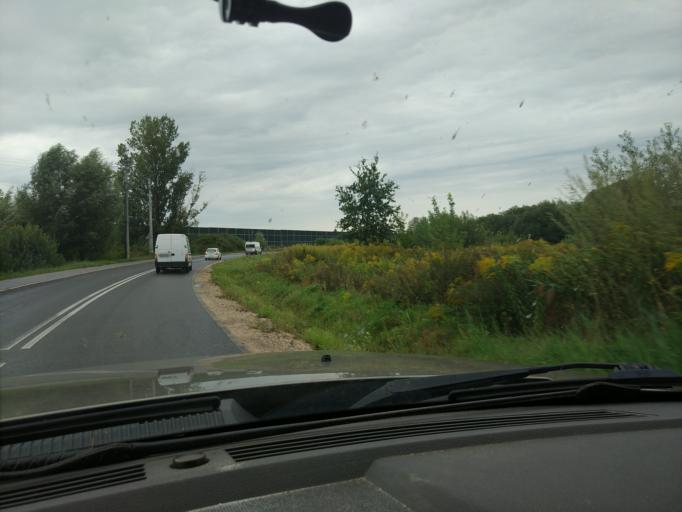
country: PL
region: Masovian Voivodeship
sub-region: Powiat pruszkowski
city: Brwinow
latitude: 52.1714
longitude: 20.7502
